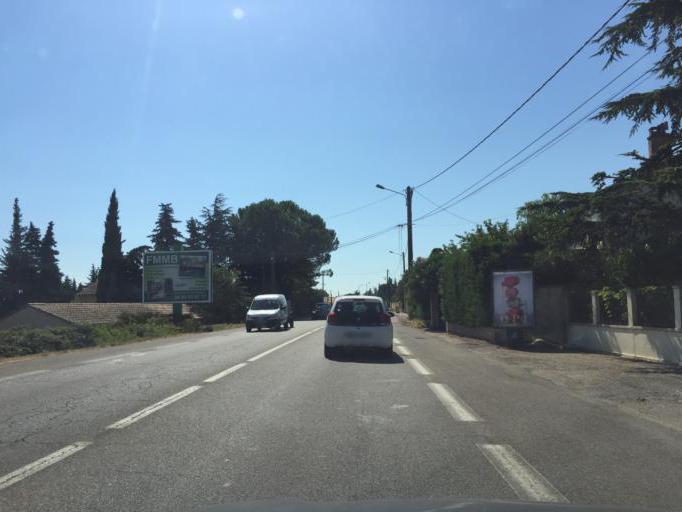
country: FR
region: Provence-Alpes-Cote d'Azur
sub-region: Departement du Vaucluse
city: Saint-Saturnin-les-Avignon
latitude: 43.9649
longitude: 4.9274
